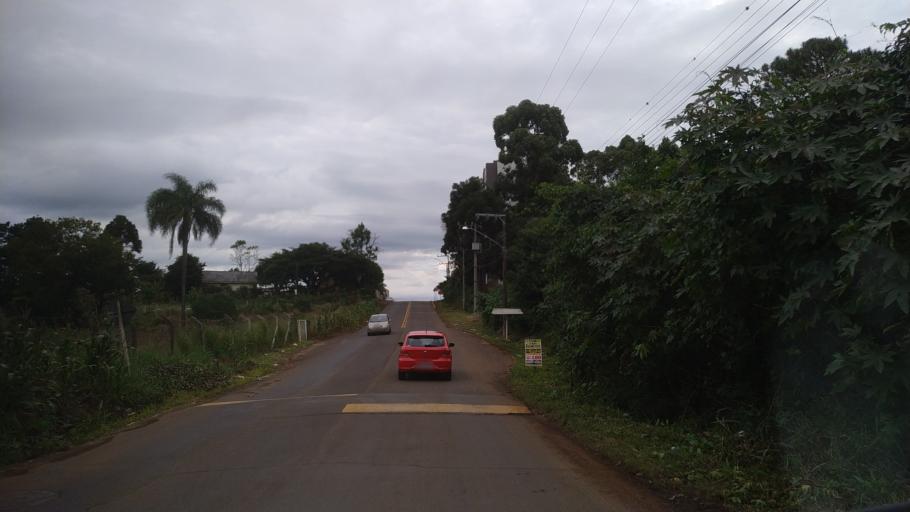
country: BR
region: Santa Catarina
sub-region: Chapeco
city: Chapeco
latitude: -27.0726
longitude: -52.6077
